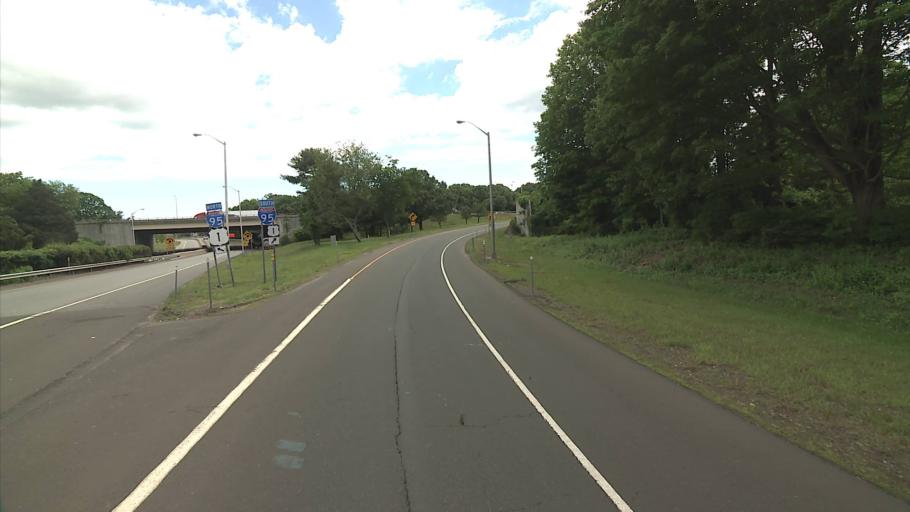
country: US
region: Connecticut
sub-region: Middlesex County
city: Old Saybrook Center
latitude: 41.3171
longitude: -72.3604
